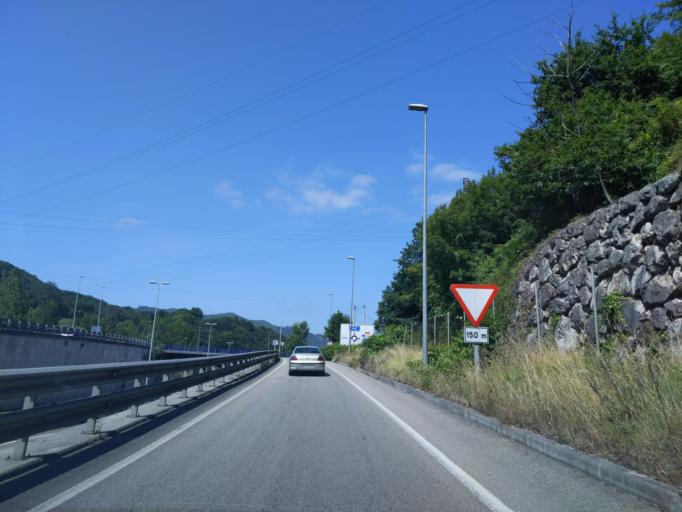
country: ES
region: Asturias
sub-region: Province of Asturias
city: Sama
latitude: 43.3218
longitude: -5.7153
